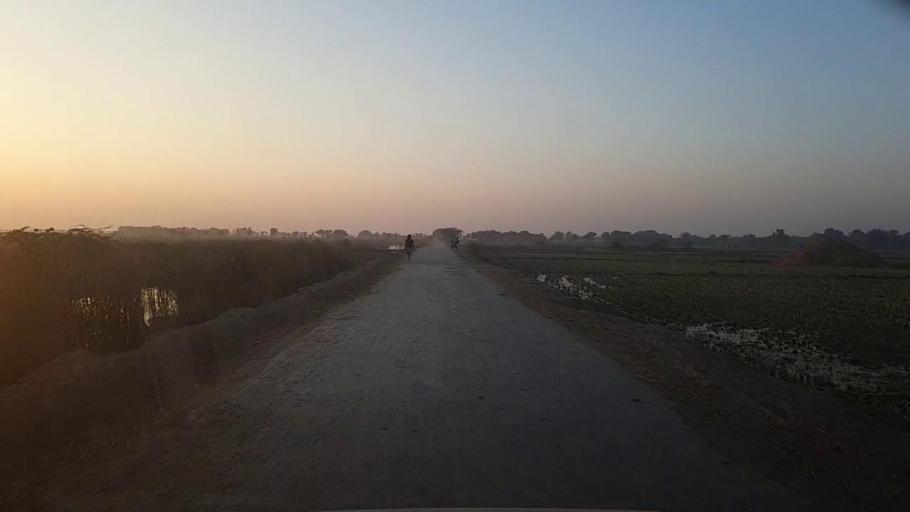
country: PK
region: Sindh
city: Khairpur Nathan Shah
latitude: 27.1554
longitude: 67.7239
